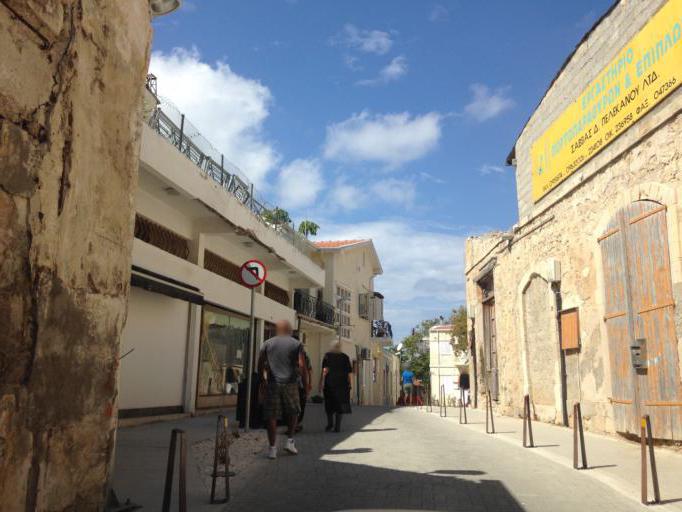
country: CY
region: Pafos
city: Paphos
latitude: 34.7798
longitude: 32.4189
